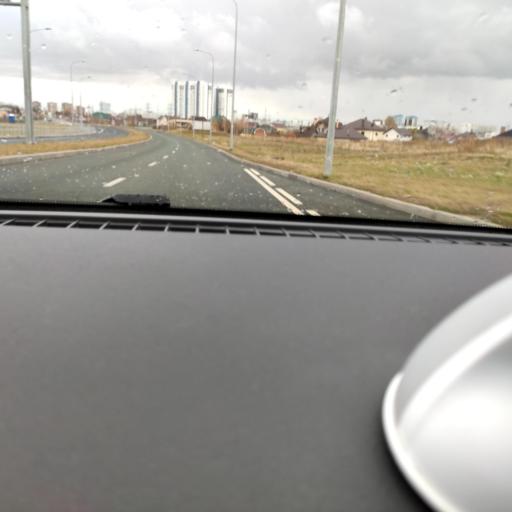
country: RU
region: Samara
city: Samara
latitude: 53.2758
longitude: 50.2317
